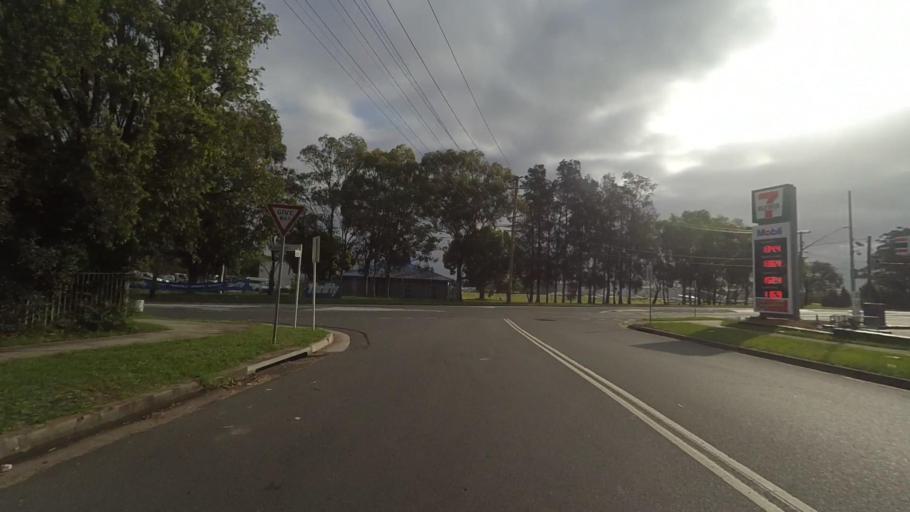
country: AU
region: New South Wales
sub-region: Bankstown
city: Milperra
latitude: -33.9155
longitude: 150.9980
